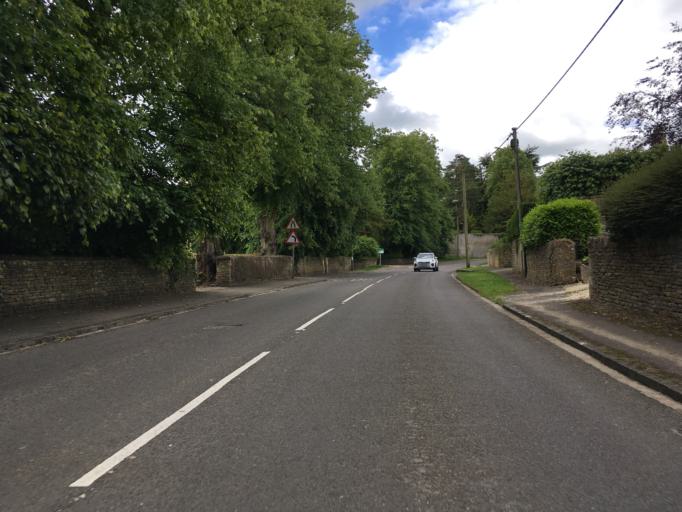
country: GB
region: England
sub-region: Oxfordshire
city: Shipton under Wychwood
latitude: 51.8573
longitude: -1.5976
